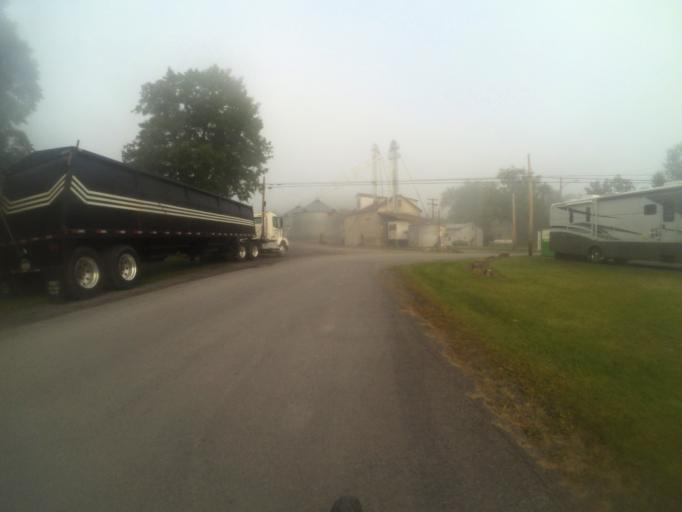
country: US
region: Pennsylvania
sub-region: Mifflin County
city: Milroy
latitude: 40.8620
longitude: -77.4640
